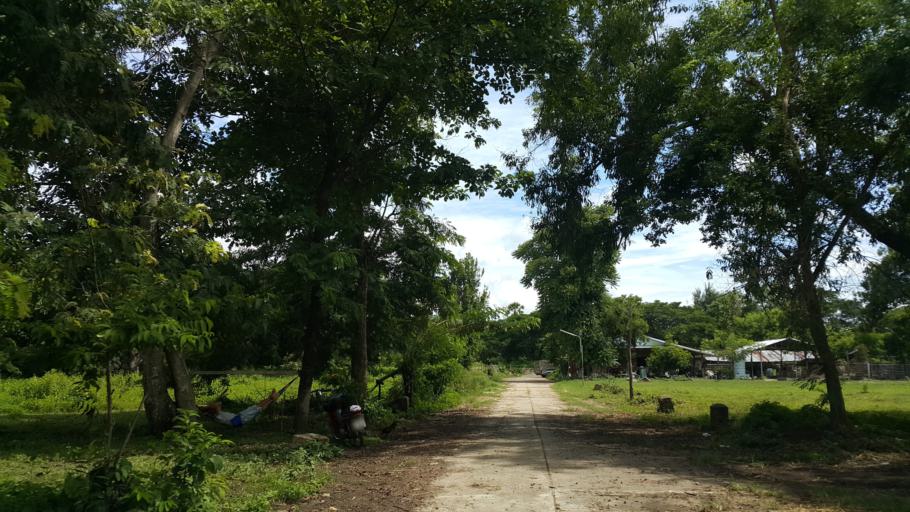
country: TH
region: Chiang Mai
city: Mae On
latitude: 18.7417
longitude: 99.2002
